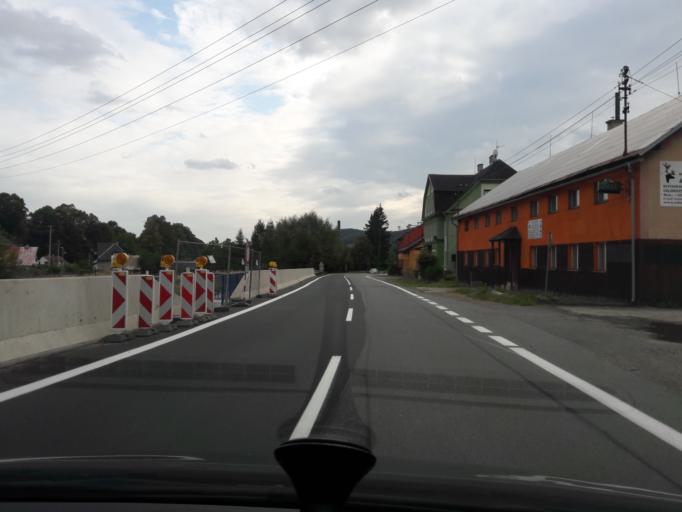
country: CZ
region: Olomoucky
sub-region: Okres Sumperk
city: Loucna nad Desnou
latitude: 50.0925
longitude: 17.0949
